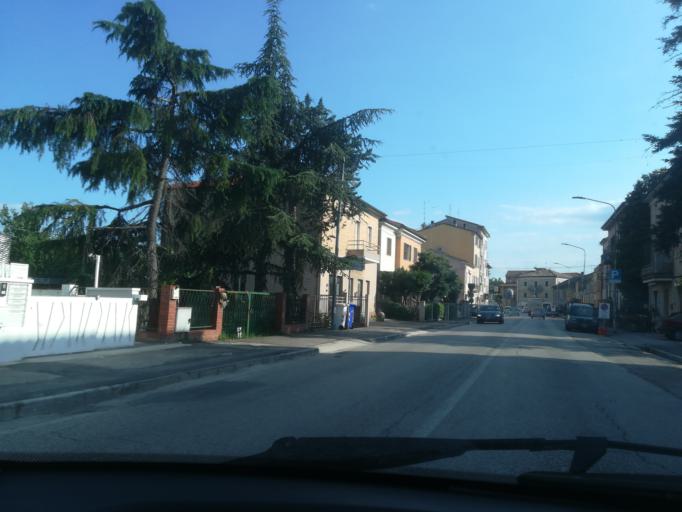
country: IT
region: The Marches
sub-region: Provincia di Macerata
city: Villa Potenza
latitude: 43.3252
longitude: 13.4266
